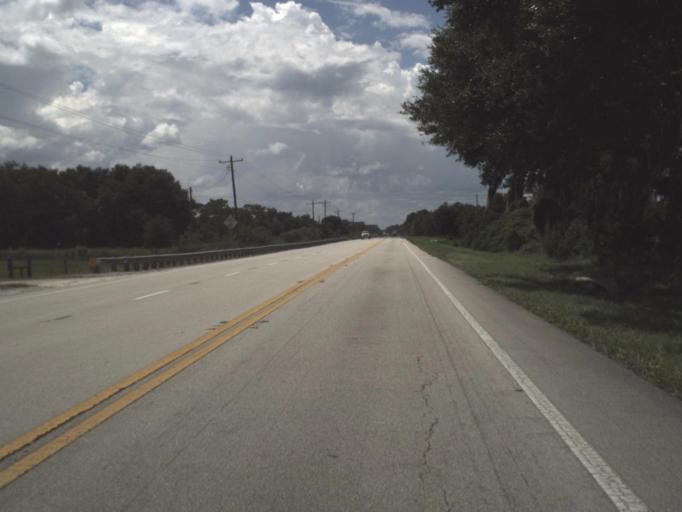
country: US
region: Florida
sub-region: Polk County
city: Babson Park
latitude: 27.8056
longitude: -81.2582
